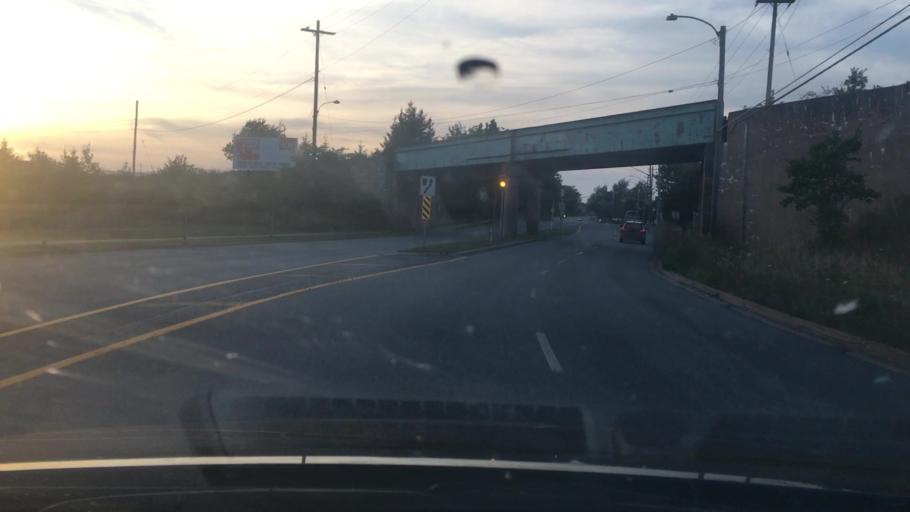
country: CA
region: Nova Scotia
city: Halifax
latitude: 44.6350
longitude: -63.5256
